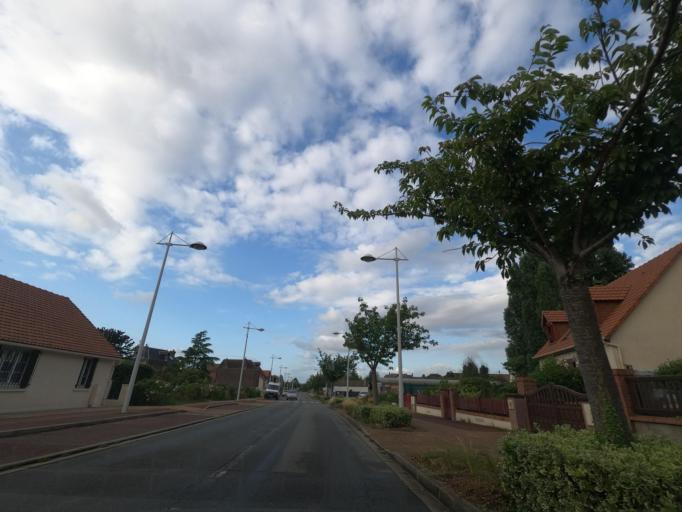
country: FR
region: Haute-Normandie
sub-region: Departement de la Seine-Maritime
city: Grand-Couronne
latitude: 49.3620
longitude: 1.0126
